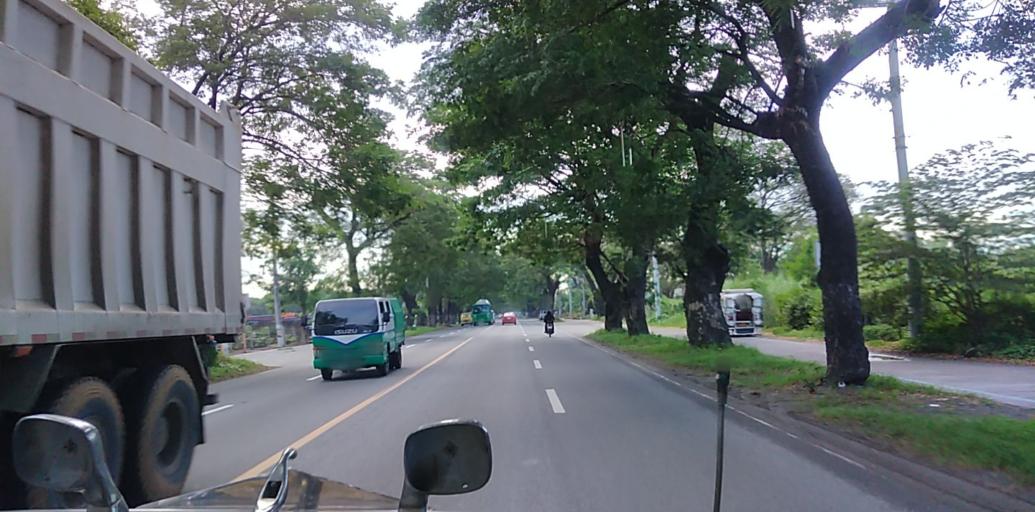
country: PH
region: Central Luzon
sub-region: Province of Pampanga
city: Telabastagan
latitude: 15.1085
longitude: 120.6138
